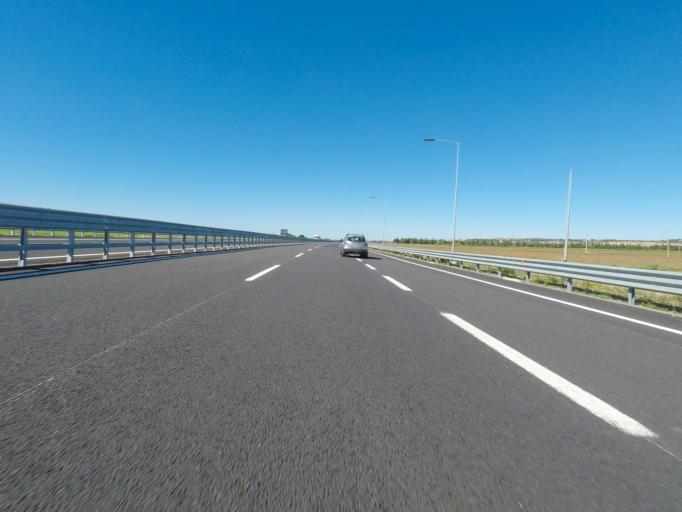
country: IT
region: Latium
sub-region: Provincia di Viterbo
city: Tarquinia
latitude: 42.2145
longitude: 11.7766
